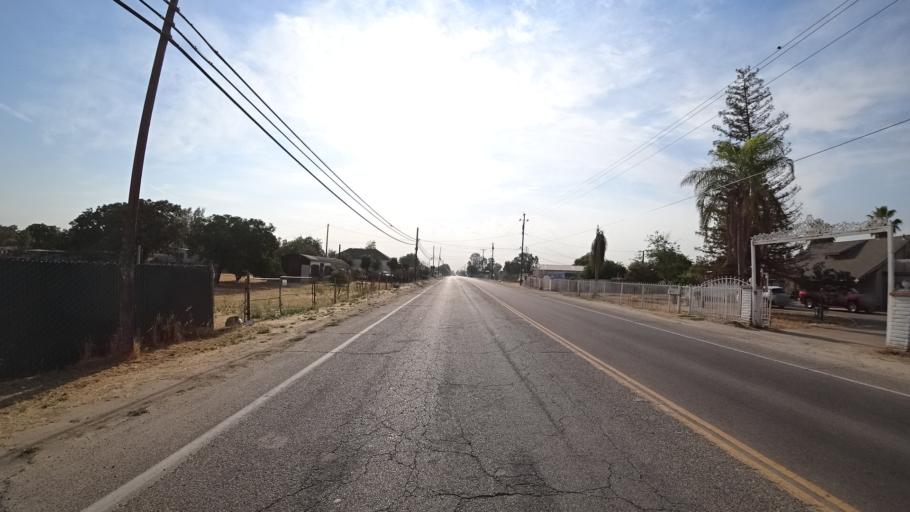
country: US
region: California
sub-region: Fresno County
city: West Park
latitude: 36.7500
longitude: -119.8548
